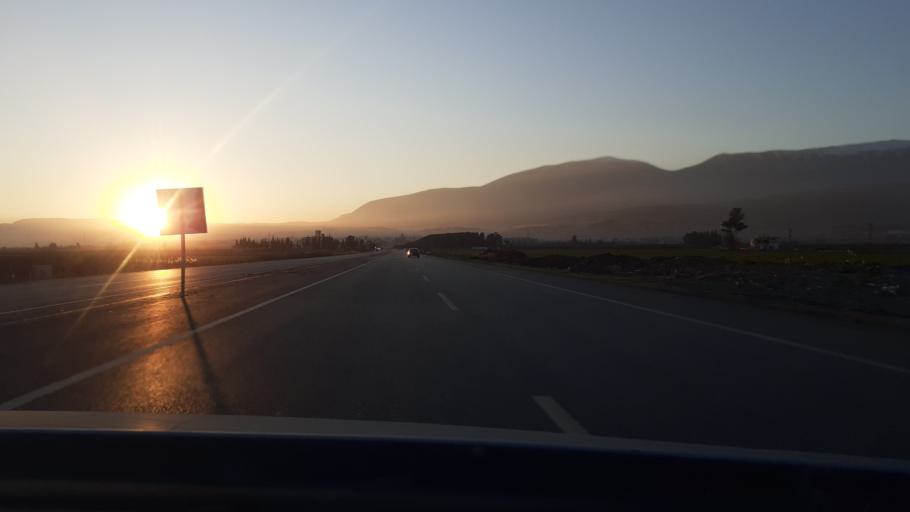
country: TR
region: Hatay
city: Kirikhan
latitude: 36.5039
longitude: 36.4040
